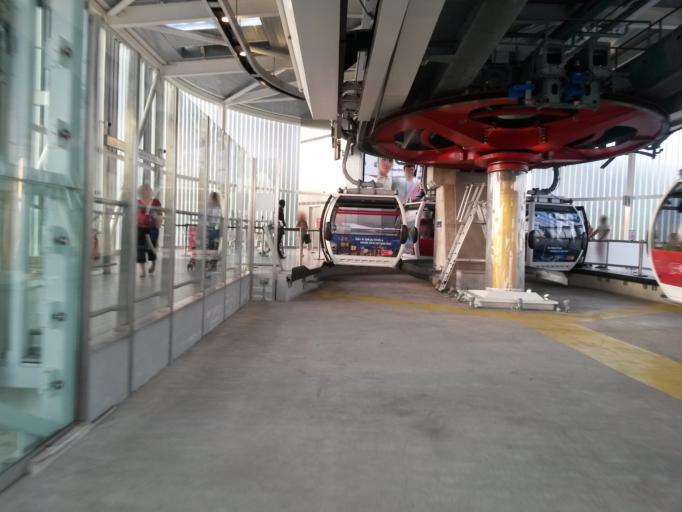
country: GB
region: England
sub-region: Greater London
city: Poplar
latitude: 51.5076
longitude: 0.0178
